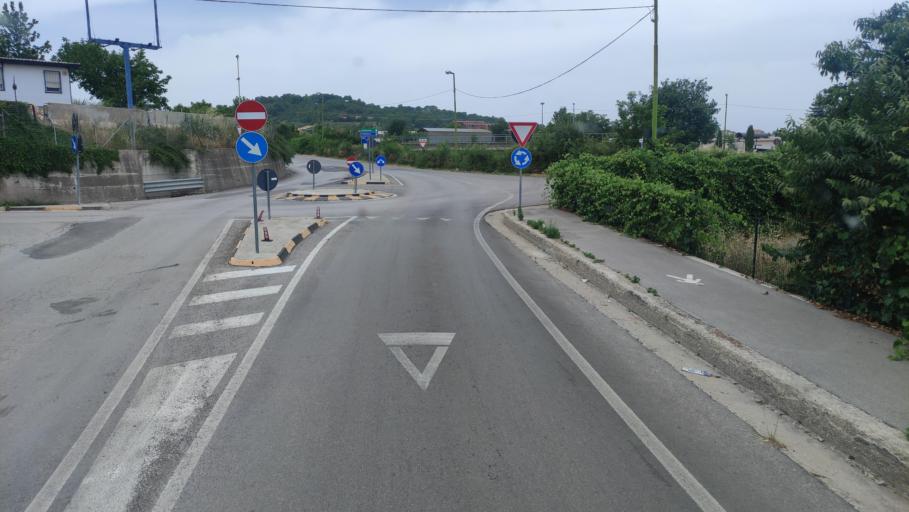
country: IT
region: Campania
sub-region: Provincia di Avellino
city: Grottaminarda
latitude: 41.0632
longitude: 15.0594
